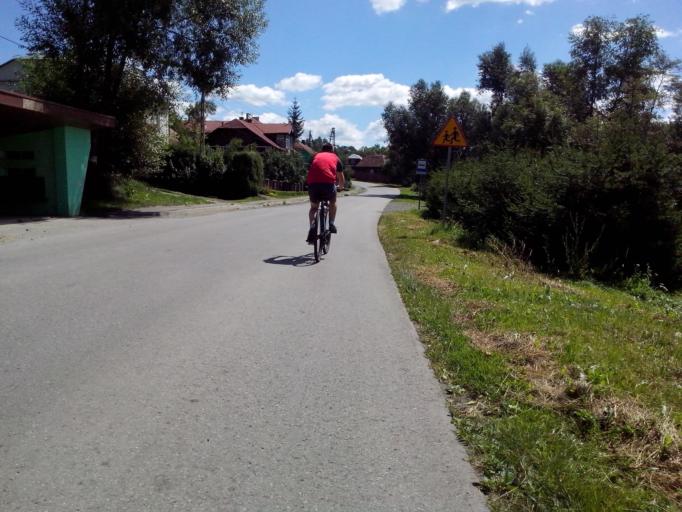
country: PL
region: Subcarpathian Voivodeship
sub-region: Powiat brzozowski
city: Blizne
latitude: 49.7885
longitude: 21.9828
